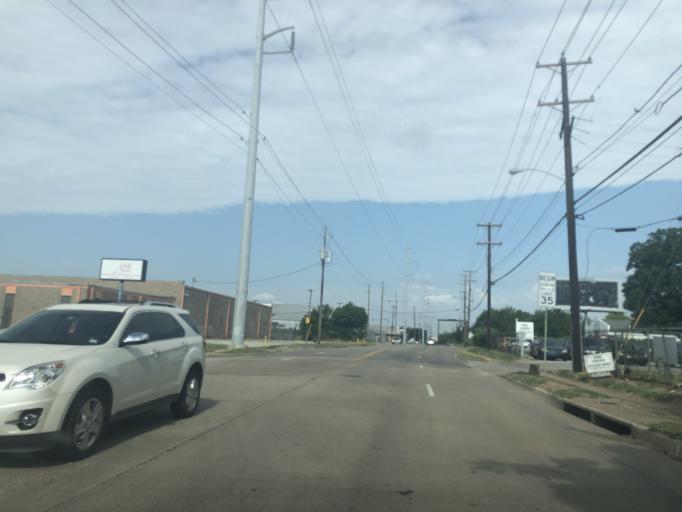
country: US
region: Texas
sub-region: Dallas County
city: University Park
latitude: 32.8263
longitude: -96.8575
